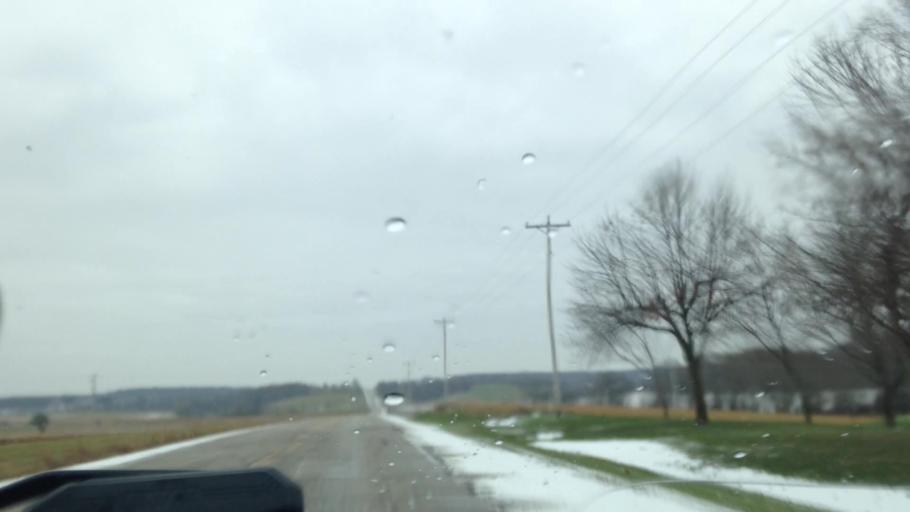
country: US
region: Wisconsin
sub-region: Dodge County
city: Mayville
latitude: 43.4729
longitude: -88.4998
